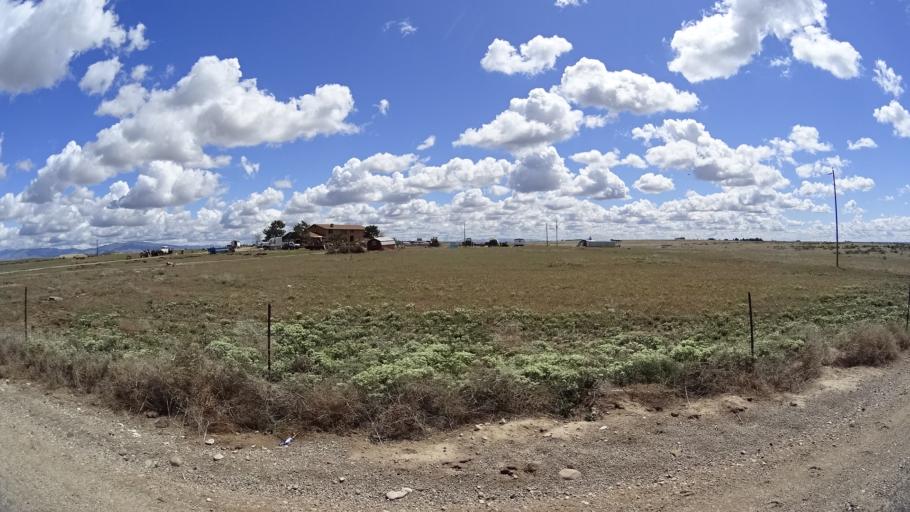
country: US
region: Idaho
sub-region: Ada County
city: Kuna
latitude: 43.4705
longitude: -116.2743
